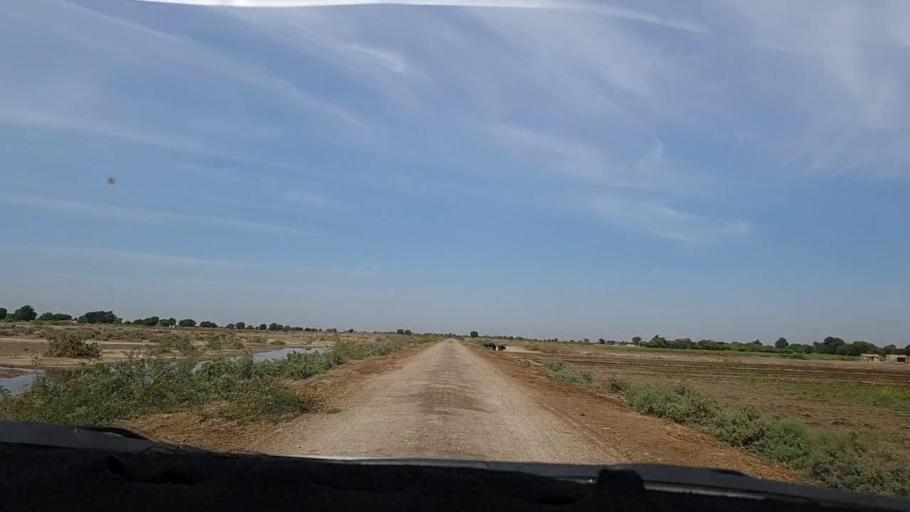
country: PK
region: Sindh
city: Pithoro
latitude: 25.4676
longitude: 69.4702
